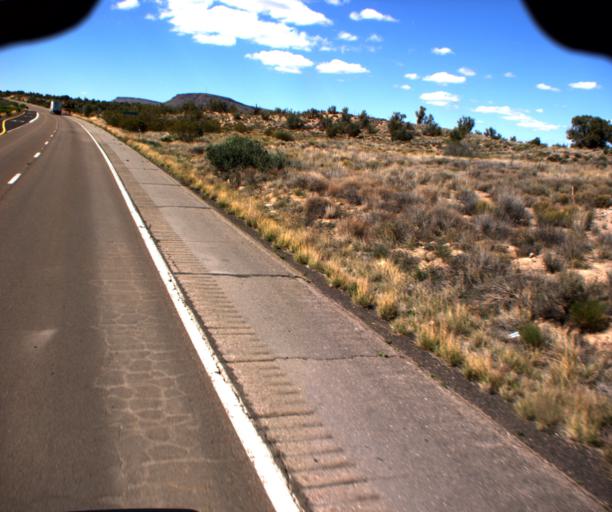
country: US
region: Arizona
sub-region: Mohave County
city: New Kingman-Butler
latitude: 35.1287
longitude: -113.6667
